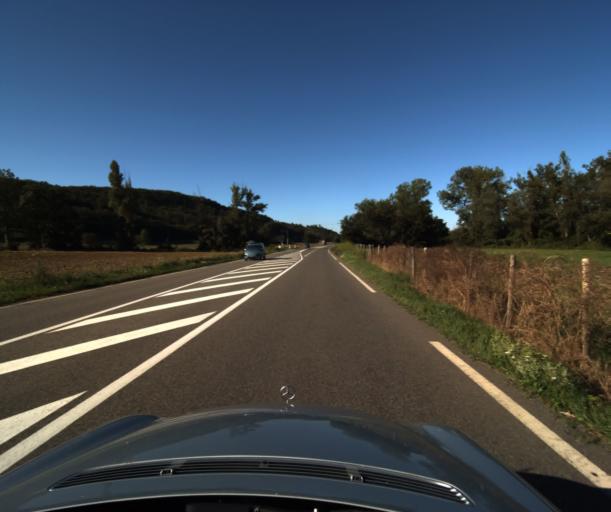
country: FR
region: Midi-Pyrenees
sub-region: Departement de l'Ariege
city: Mirepoix
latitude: 43.0066
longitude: 1.8843
